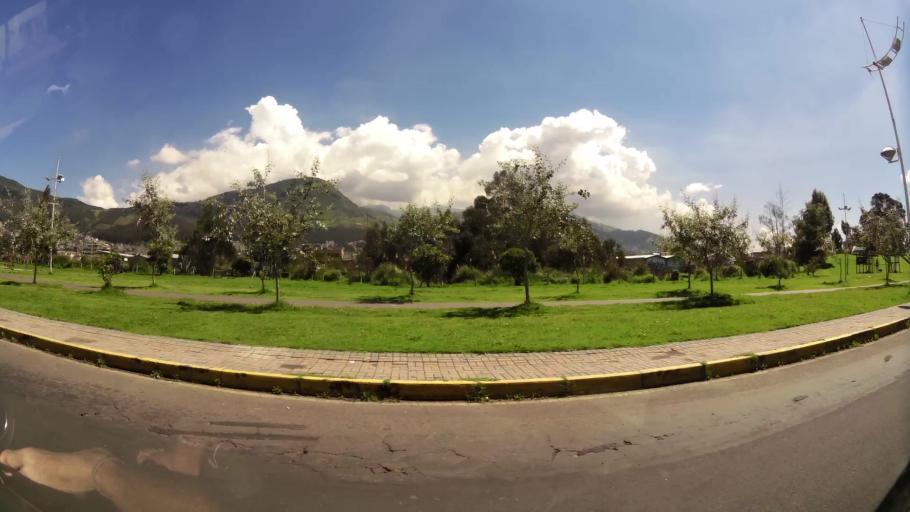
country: EC
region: Pichincha
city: Quito
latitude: -0.2661
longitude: -78.5428
